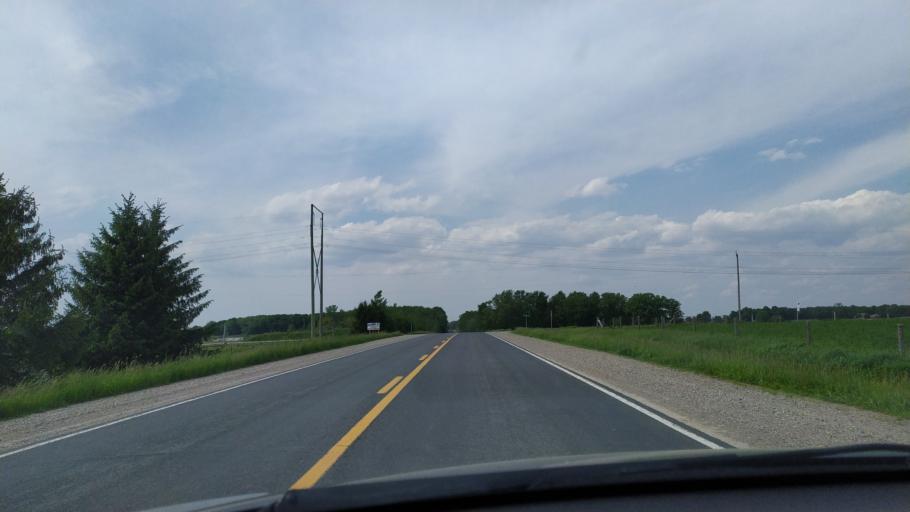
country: CA
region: Ontario
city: Ingersoll
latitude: 43.0372
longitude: -80.9765
